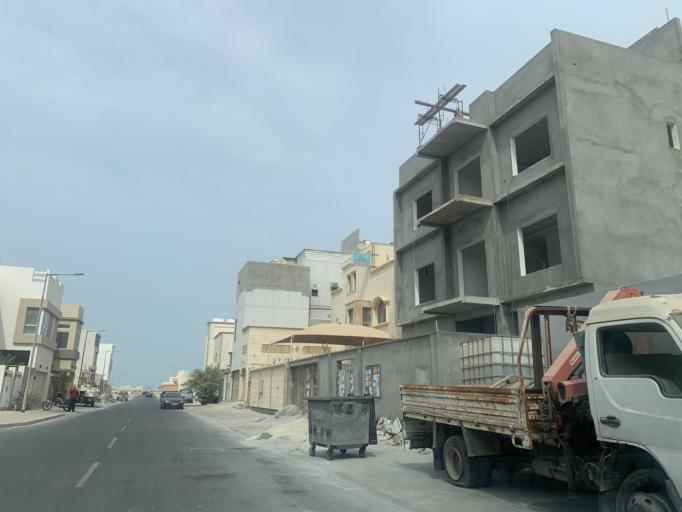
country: BH
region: Muharraq
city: Al Muharraq
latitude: 26.2859
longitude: 50.6352
